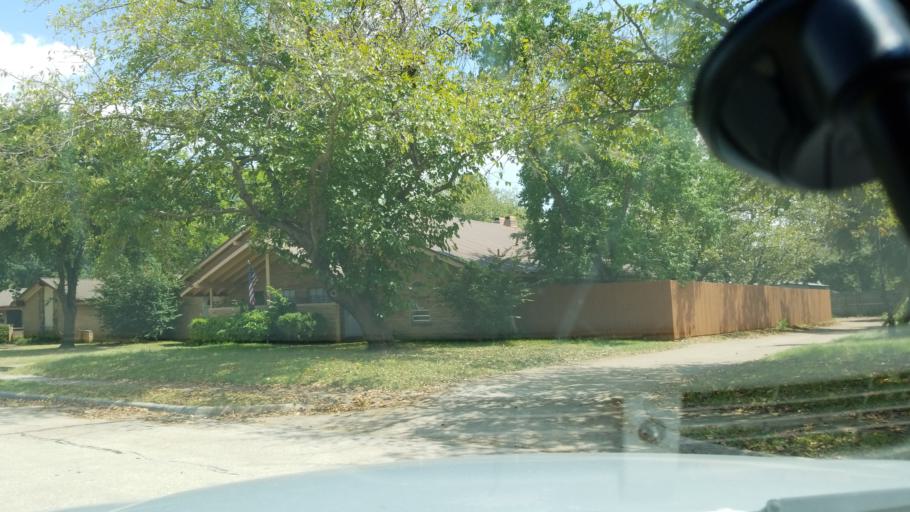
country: US
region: Texas
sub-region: Dallas County
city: Irving
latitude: 32.8187
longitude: -96.9877
